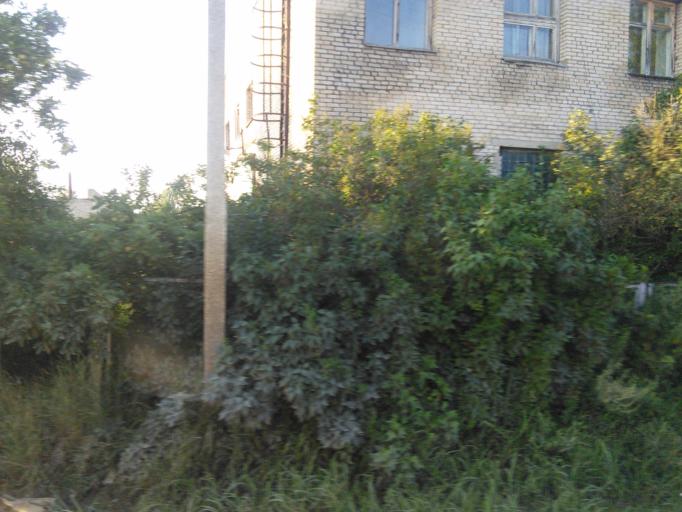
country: RU
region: Vologda
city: Chagoda
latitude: 59.1603
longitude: 35.3236
